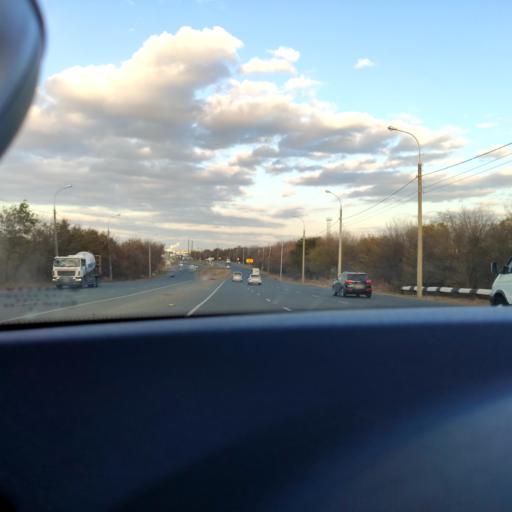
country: RU
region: Samara
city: Smyshlyayevka
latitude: 53.2543
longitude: 50.3681
